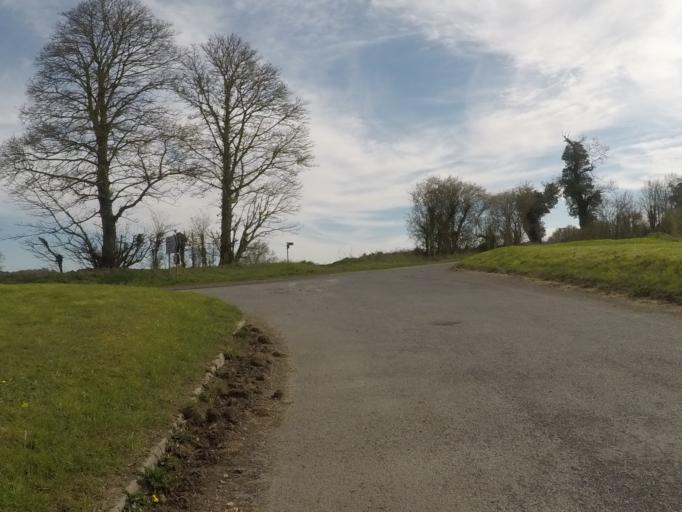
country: GB
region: England
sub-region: Oxfordshire
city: Charlbury
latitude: 51.8511
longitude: -1.4727
